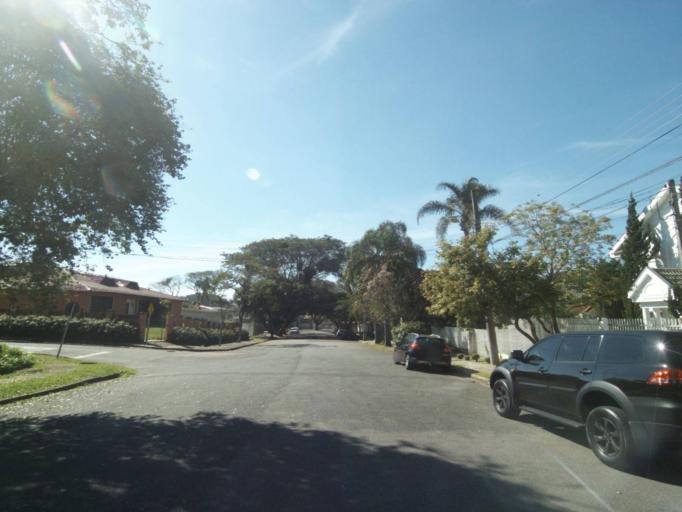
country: BR
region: Parana
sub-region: Curitiba
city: Curitiba
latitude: -25.4173
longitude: -49.2363
